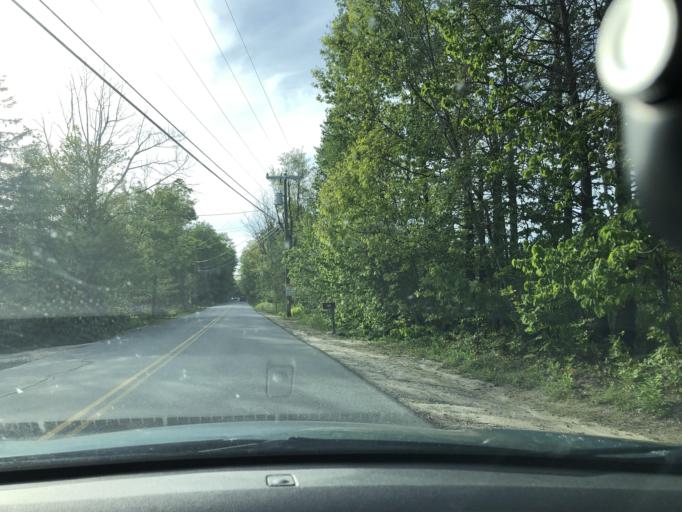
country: US
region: New Hampshire
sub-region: Merrimack County
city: New London
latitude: 43.4069
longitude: -71.9557
